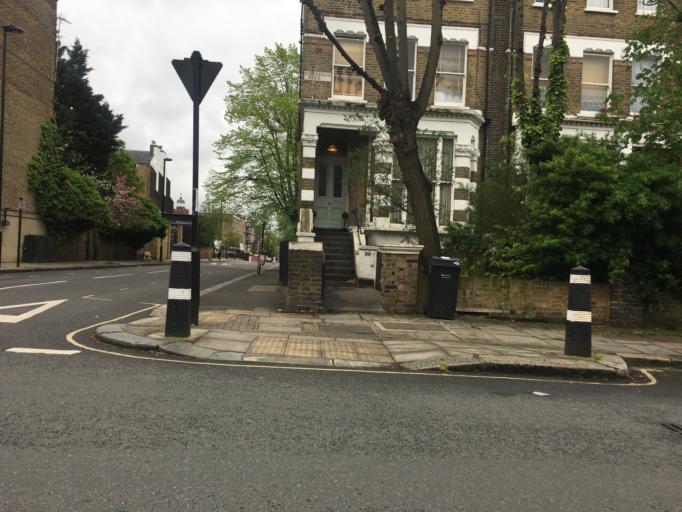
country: GB
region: England
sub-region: Greater London
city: Holloway
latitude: 51.5485
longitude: -0.1351
